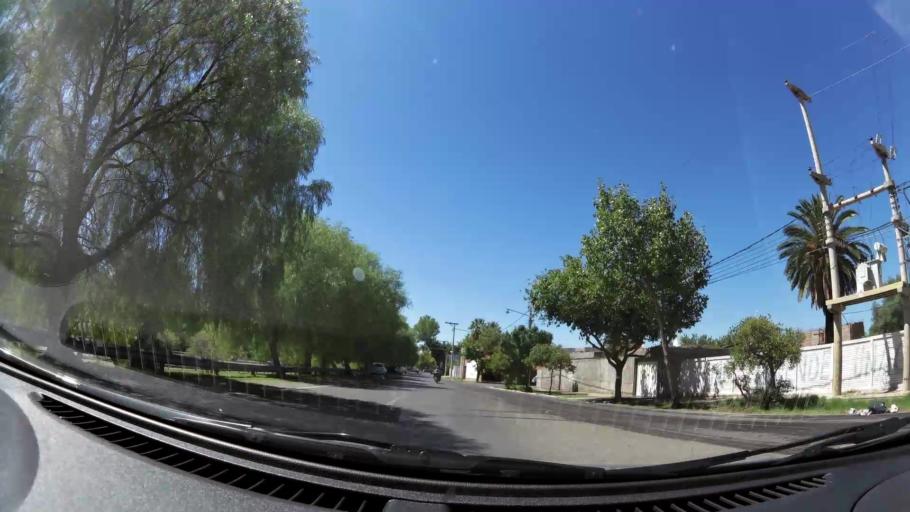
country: AR
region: San Juan
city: San Juan
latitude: -31.5241
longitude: -68.5479
